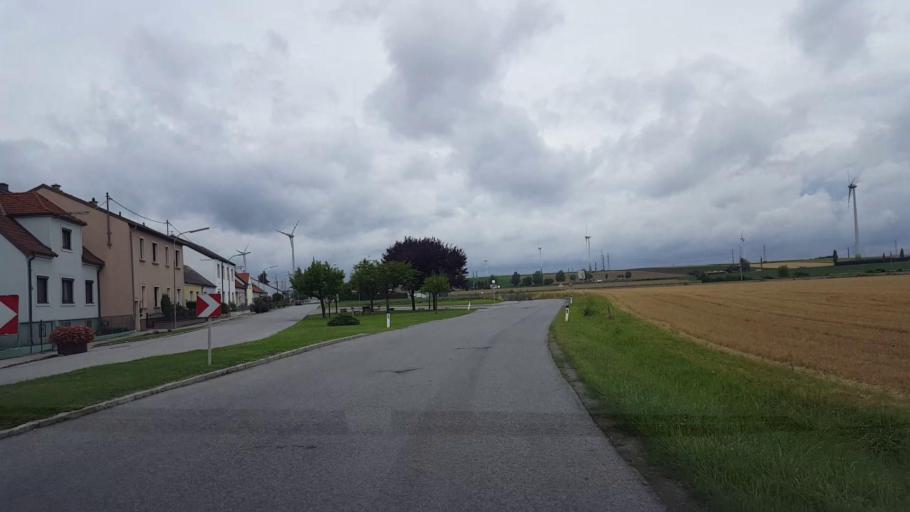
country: AT
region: Lower Austria
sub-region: Politischer Bezirk Bruck an der Leitha
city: Bruck an der Leitha
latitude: 48.0197
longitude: 16.7201
